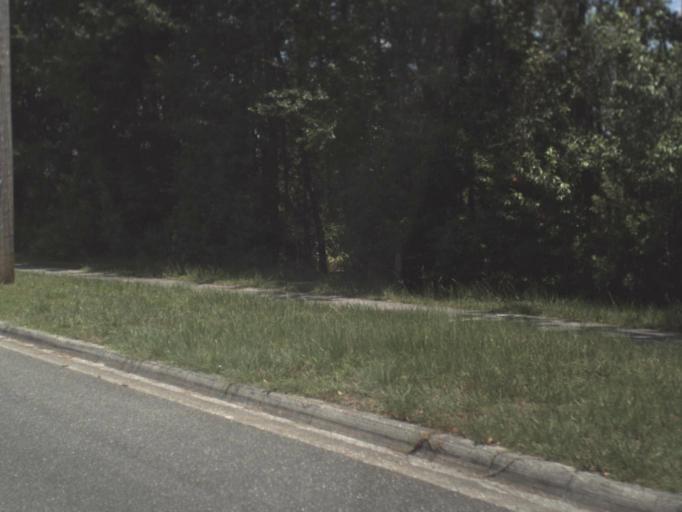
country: US
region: Florida
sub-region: Bradford County
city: Starke
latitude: 29.9637
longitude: -82.1184
